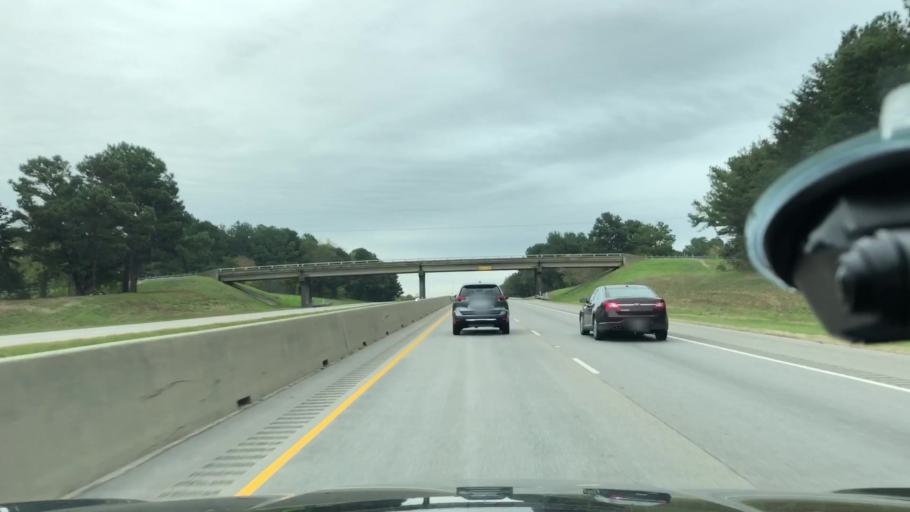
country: US
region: Texas
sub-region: Franklin County
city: Mount Vernon
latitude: 33.1611
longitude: -95.1335
